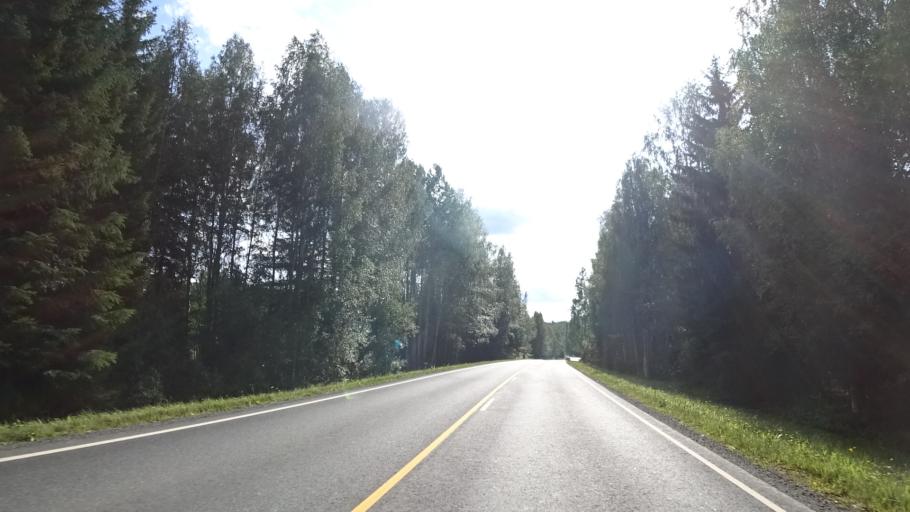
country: FI
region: North Karelia
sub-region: Keski-Karjala
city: Tohmajaervi
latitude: 62.2117
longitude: 30.2921
